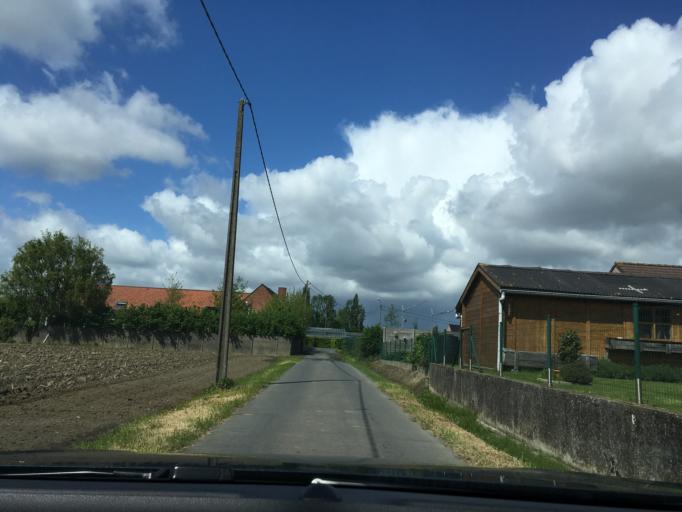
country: BE
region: Flanders
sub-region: Provincie West-Vlaanderen
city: Hooglede
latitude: 50.9929
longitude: 3.0950
